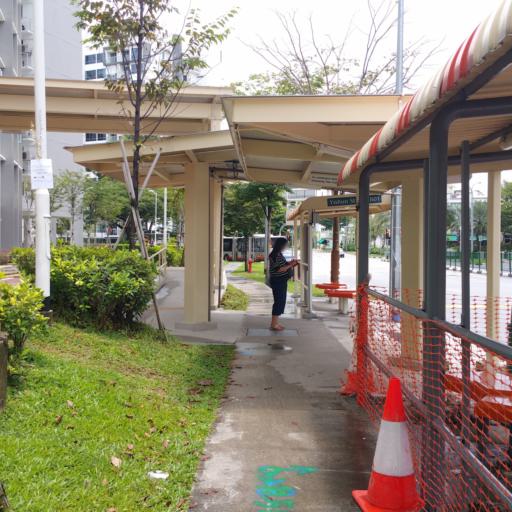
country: MY
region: Johor
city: Kampung Pasir Gudang Baru
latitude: 1.4192
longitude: 103.8461
